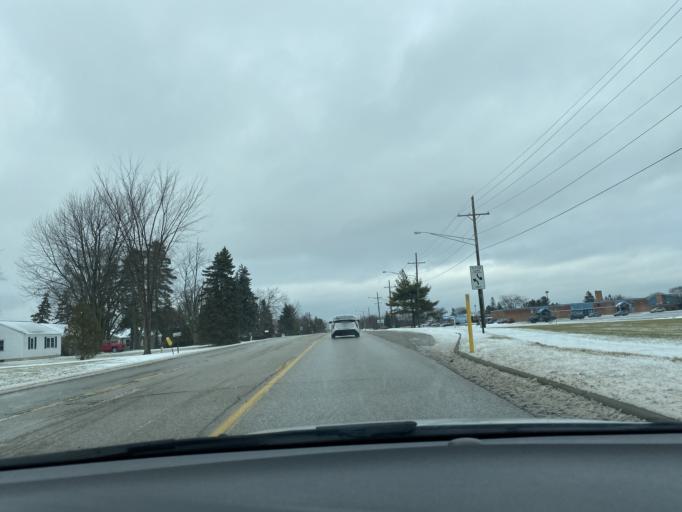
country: US
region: Michigan
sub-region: Lapeer County
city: Lapeer
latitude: 43.0530
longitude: -83.3426
